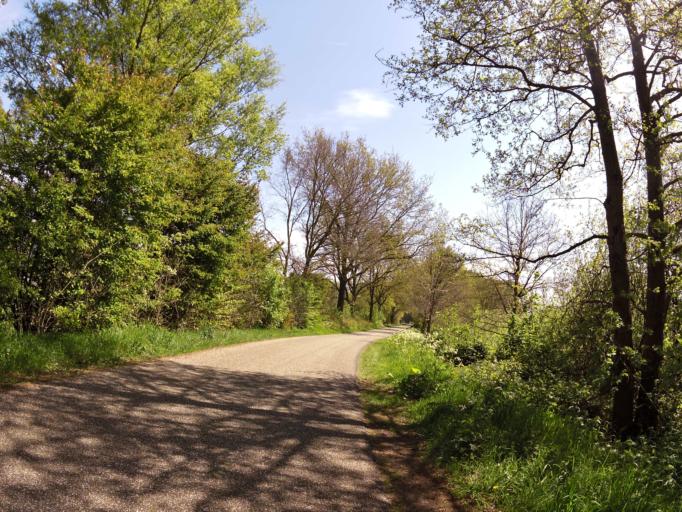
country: NL
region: North Brabant
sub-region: Gemeente Sint-Michielsgestel
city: Sint-Michielsgestel
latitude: 51.6725
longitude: 5.3991
